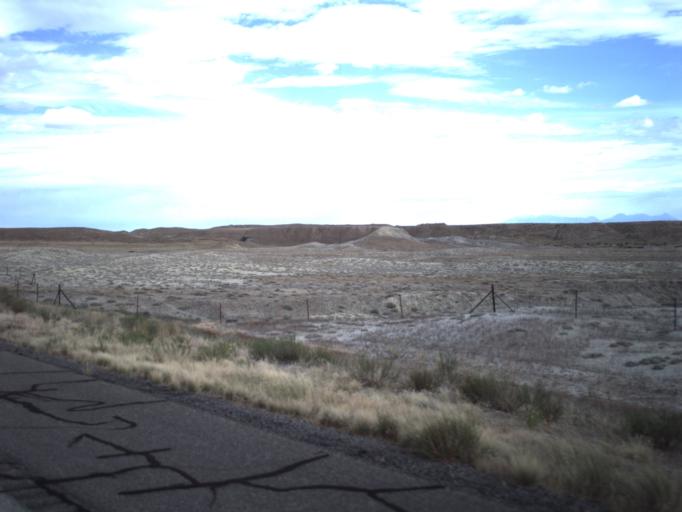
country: US
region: Utah
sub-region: Grand County
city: Moab
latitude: 38.9331
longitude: -109.8560
